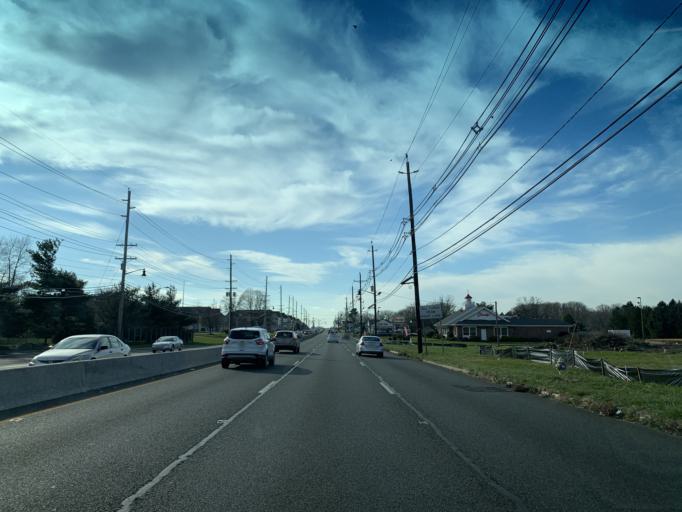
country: US
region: New Jersey
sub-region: Burlington County
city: Cinnaminson
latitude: 39.9941
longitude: -74.9985
